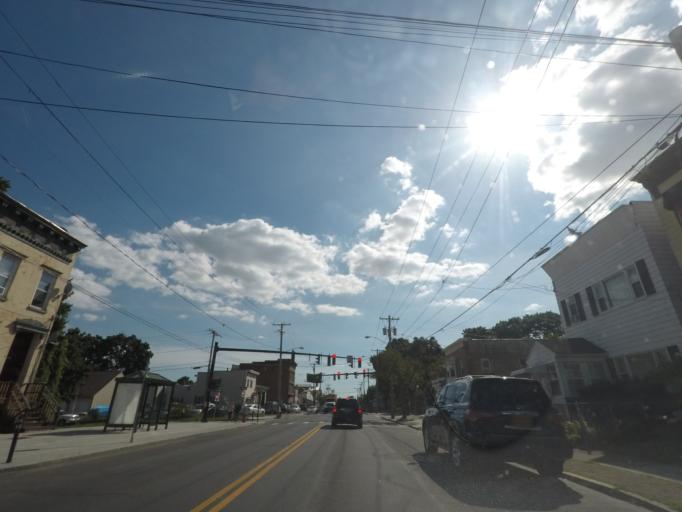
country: US
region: New York
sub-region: Albany County
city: Menands
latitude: 42.6725
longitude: -73.7379
